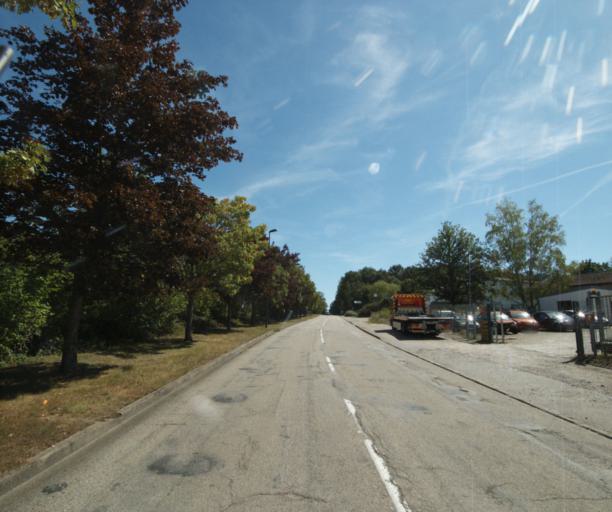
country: FR
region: Lorraine
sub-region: Departement des Vosges
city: Golbey
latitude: 48.2024
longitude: 6.4591
